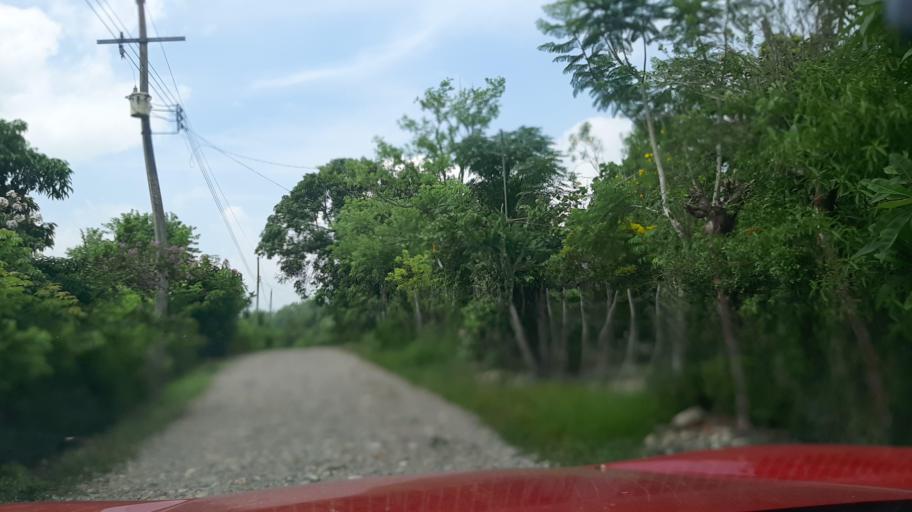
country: MX
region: Veracruz
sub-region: Papantla
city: Polutla
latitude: 20.4486
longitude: -97.2430
